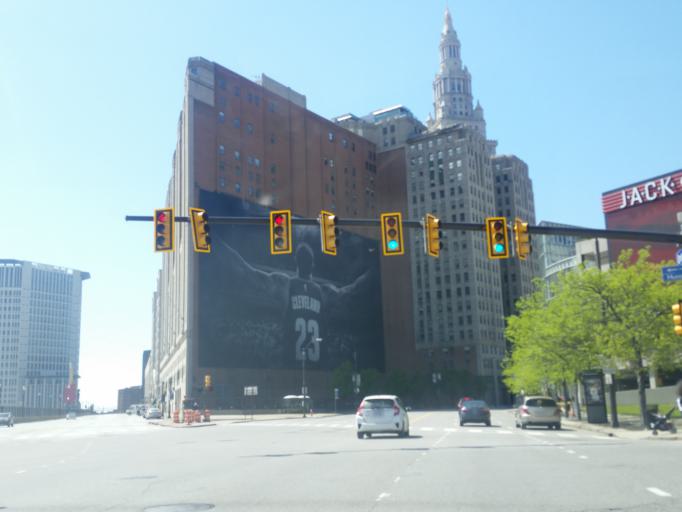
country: US
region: Ohio
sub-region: Cuyahoga County
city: Cleveland
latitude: 41.4965
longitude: -81.6900
